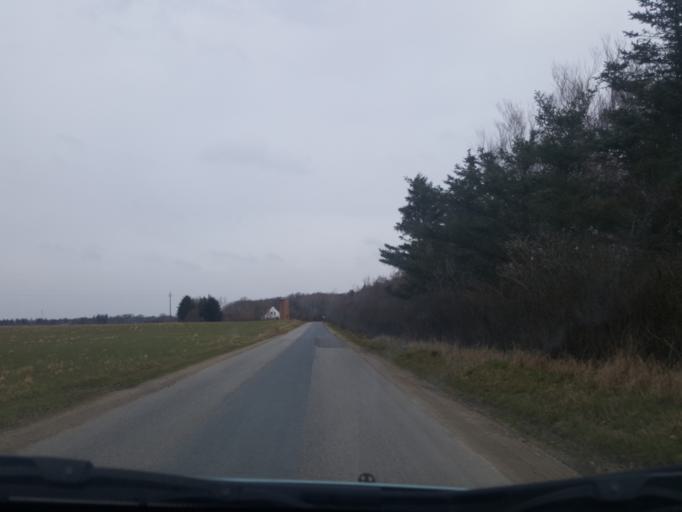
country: DK
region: Central Jutland
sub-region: Holstebro Kommune
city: Ulfborg
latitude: 56.2205
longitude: 8.2635
